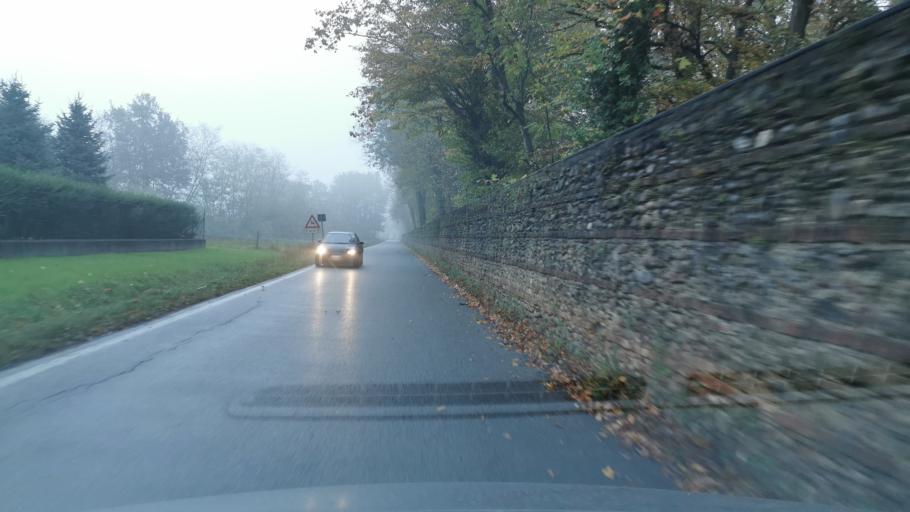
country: IT
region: Piedmont
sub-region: Provincia di Torino
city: Aglie
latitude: 45.3648
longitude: 7.7742
